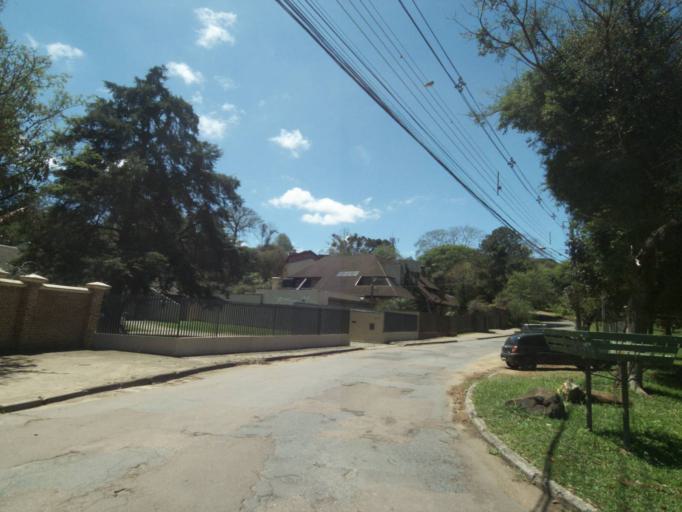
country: BR
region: Parana
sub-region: Curitiba
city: Curitiba
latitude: -25.3815
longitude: -49.2668
